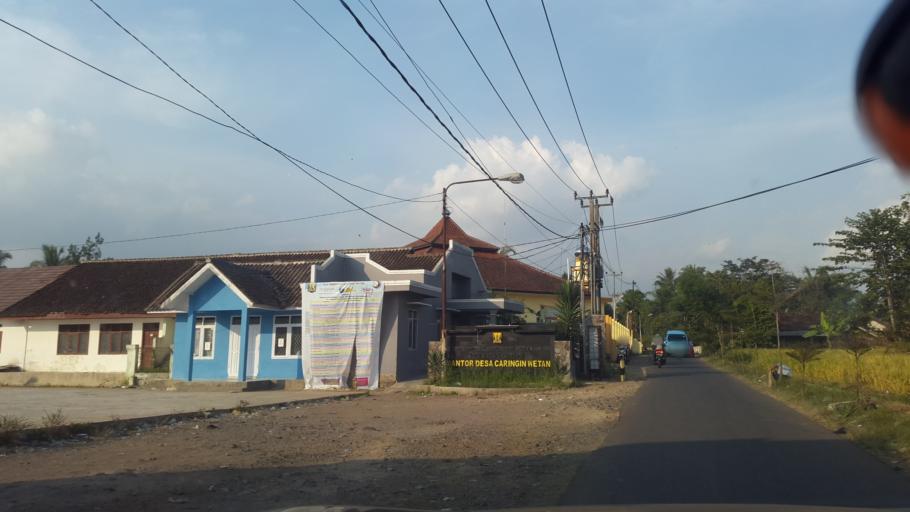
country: ID
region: West Java
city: Sukabumi
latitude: -6.8732
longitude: 106.8698
